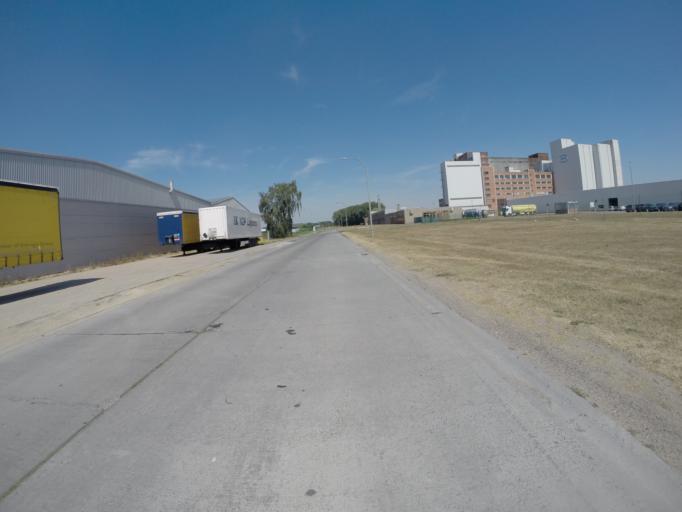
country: BE
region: Flanders
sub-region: Provincie Oost-Vlaanderen
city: Aalter
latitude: 51.1069
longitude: 3.4462
